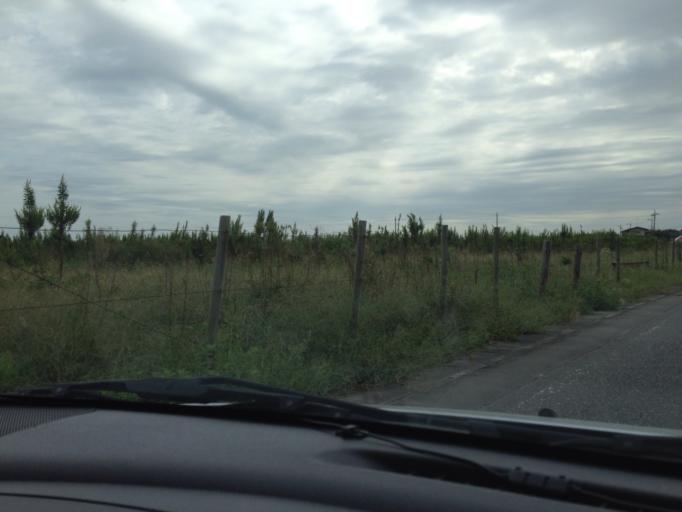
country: JP
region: Ibaraki
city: Ami
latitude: 36.0392
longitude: 140.2380
